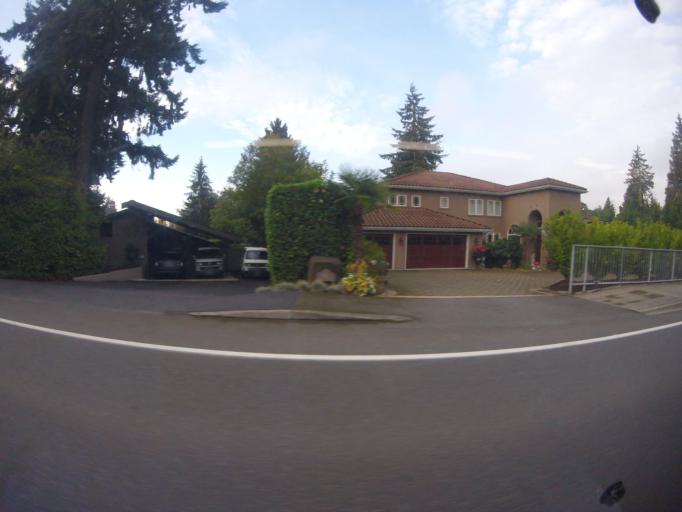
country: US
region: Washington
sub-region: King County
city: Medina
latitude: 47.6176
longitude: -122.2191
